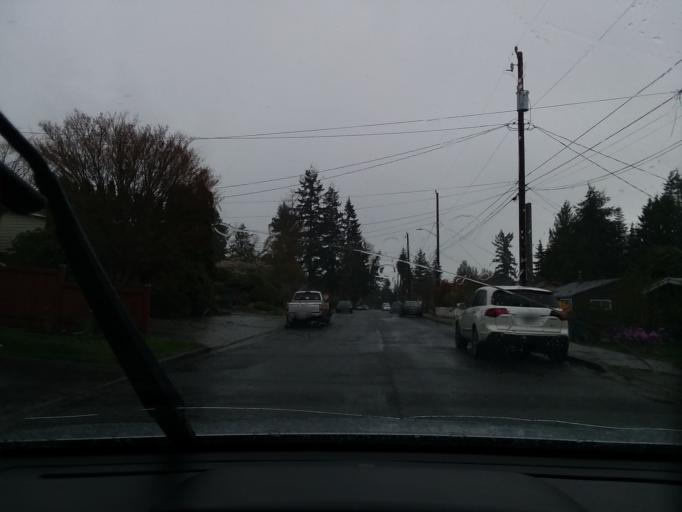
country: US
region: Washington
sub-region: King County
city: Shoreline
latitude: 47.7583
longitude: -122.3175
